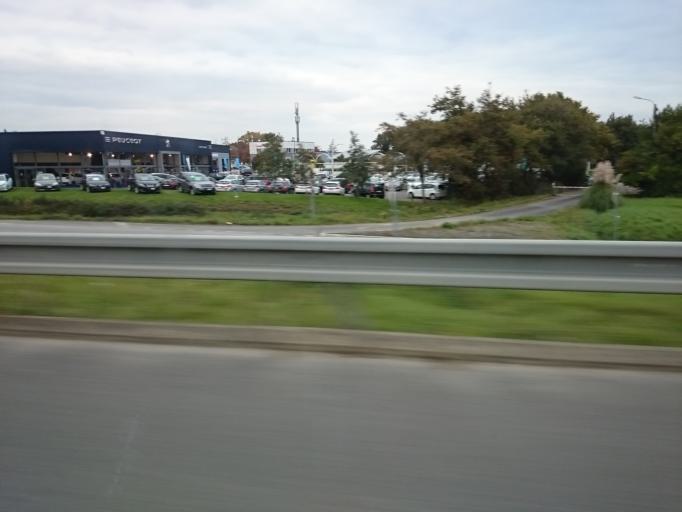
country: FR
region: Brittany
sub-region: Departement du Morbihan
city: Auray
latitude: 47.6649
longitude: -3.0108
